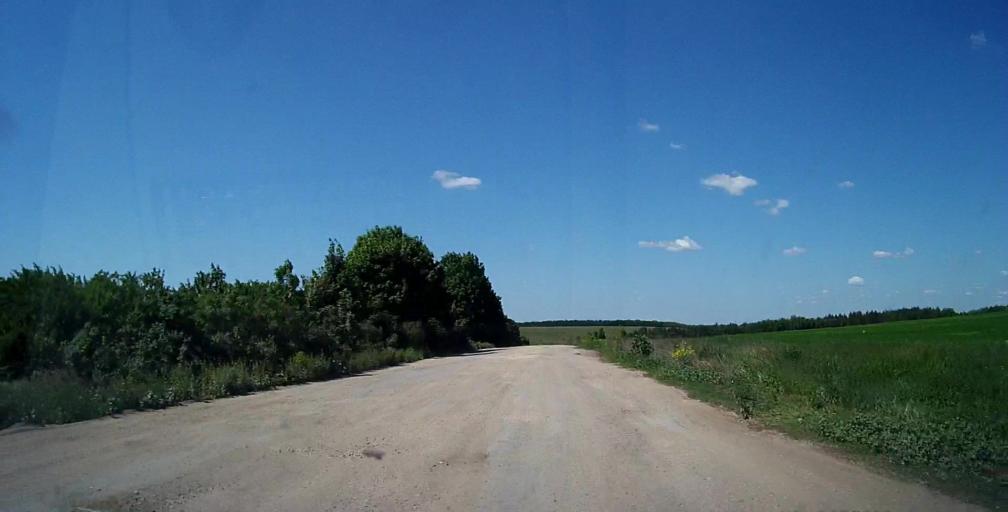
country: RU
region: Tula
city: Kurkino
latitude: 53.2006
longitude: 38.5846
